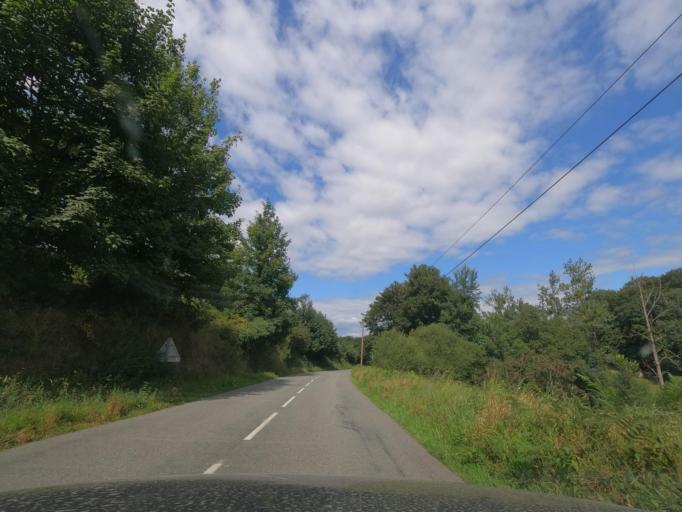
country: FR
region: Pays de la Loire
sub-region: Departement de la Mayenne
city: Landivy
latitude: 48.4519
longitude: -1.0667
